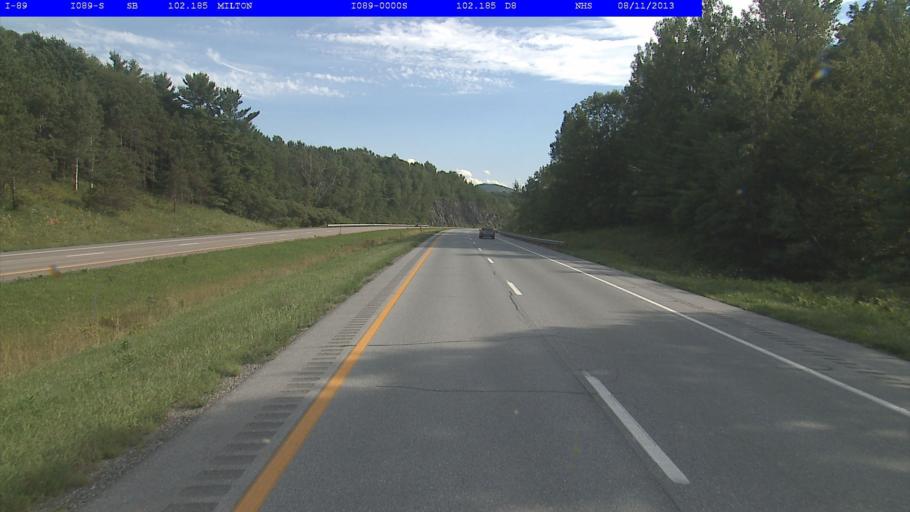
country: US
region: Vermont
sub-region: Chittenden County
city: Milton
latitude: 44.6447
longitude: -73.1399
